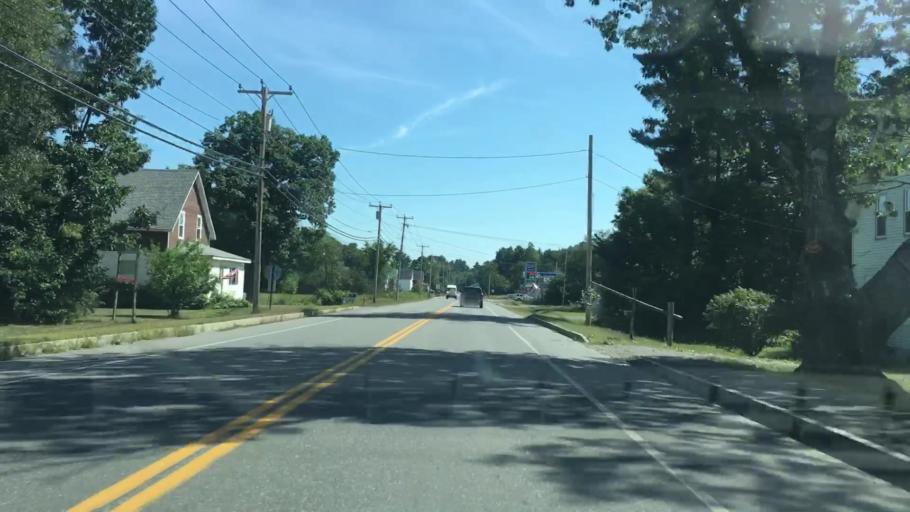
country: US
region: Maine
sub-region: Piscataquis County
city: Milo
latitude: 45.2466
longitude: -68.9775
